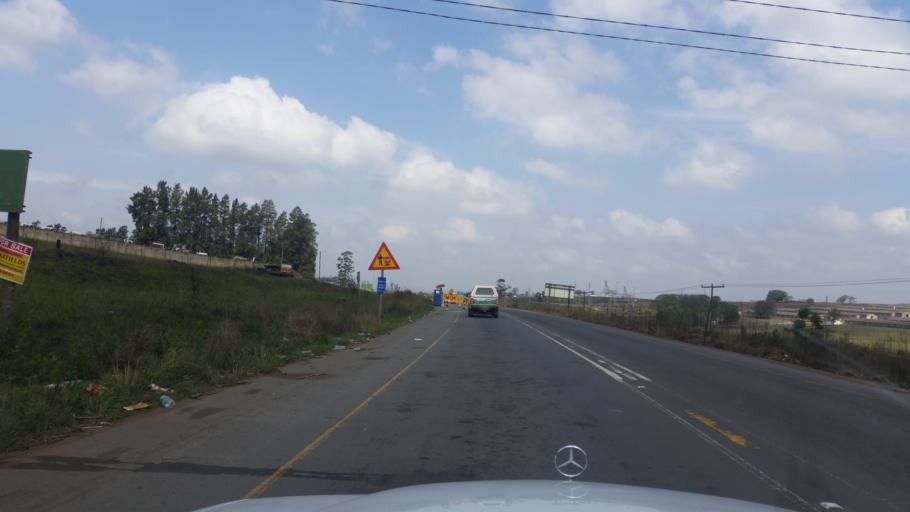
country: ZA
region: KwaZulu-Natal
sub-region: uMgungundlovu District Municipality
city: Camperdown
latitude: -29.7268
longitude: 30.5002
